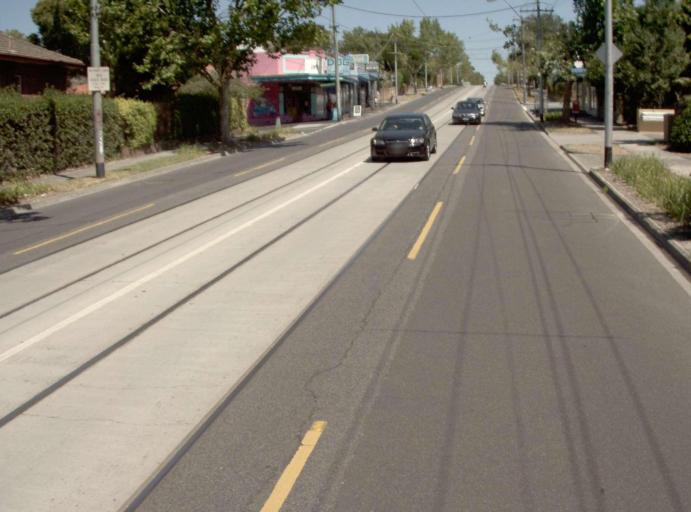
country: AU
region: Victoria
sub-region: Boroondara
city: Canterbury
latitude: -37.8352
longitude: 145.0920
